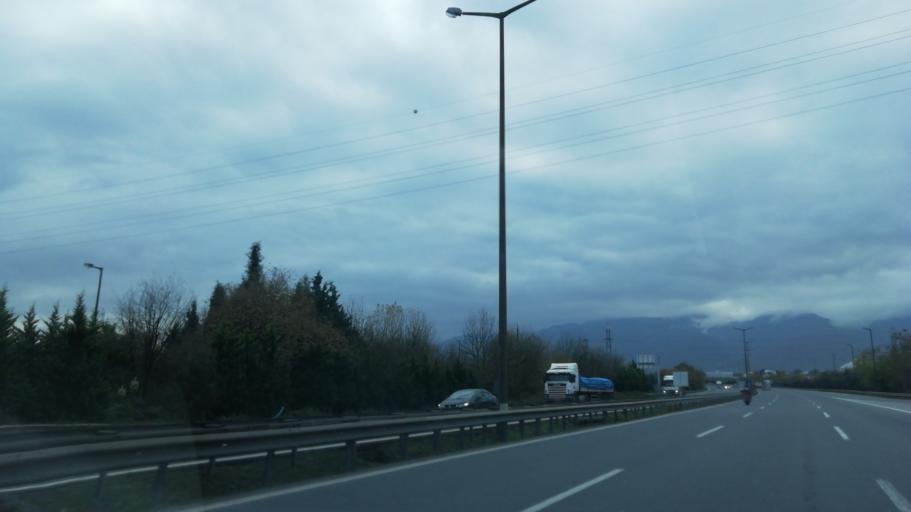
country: TR
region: Kocaeli
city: Kosekoy
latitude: 40.7466
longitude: 30.0415
